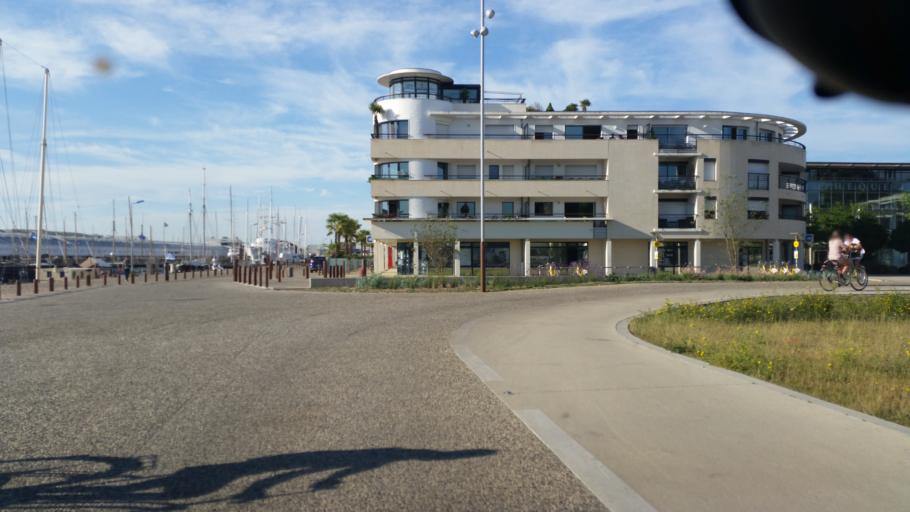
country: FR
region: Poitou-Charentes
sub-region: Departement de la Charente-Maritime
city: La Rochelle
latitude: 46.1542
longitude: -1.1526
